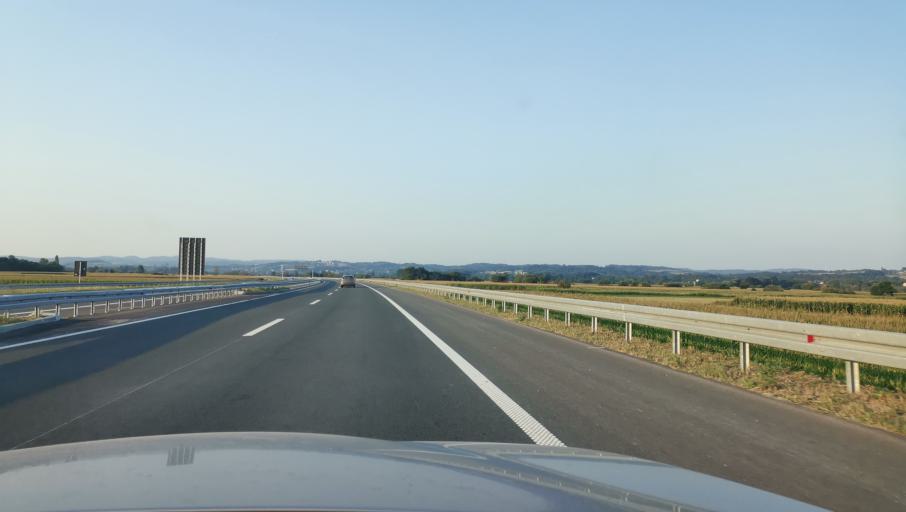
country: RS
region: Central Serbia
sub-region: Kolubarski Okrug
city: Ljig
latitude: 44.2457
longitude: 20.2662
